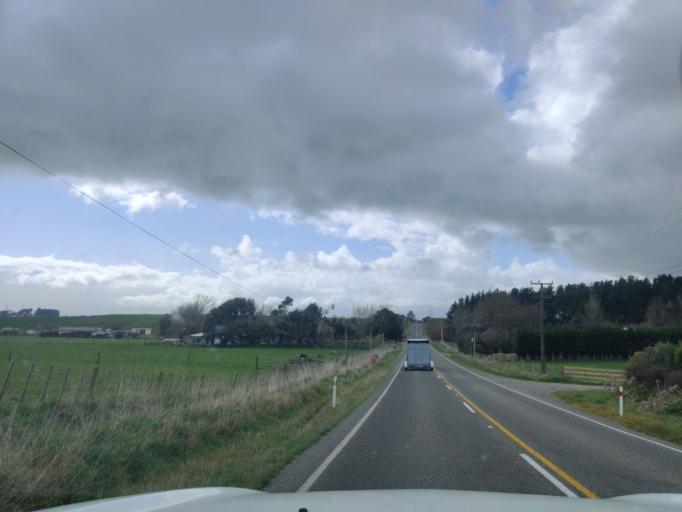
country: NZ
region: Manawatu-Wanganui
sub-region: Palmerston North City
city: Palmerston North
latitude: -40.4461
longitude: 175.5456
